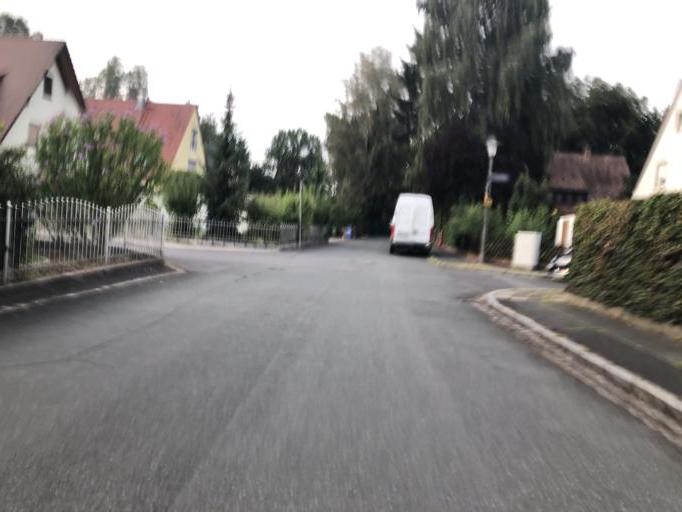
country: DE
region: Bavaria
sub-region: Regierungsbezirk Mittelfranken
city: Erlangen
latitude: 49.5540
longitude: 11.0255
